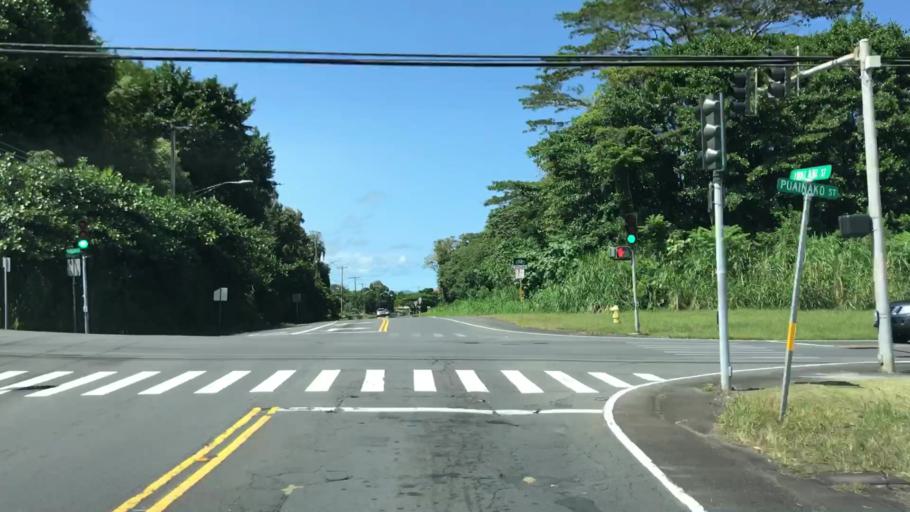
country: US
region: Hawaii
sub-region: Hawaii County
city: Hilo
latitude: 19.6938
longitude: -155.0813
